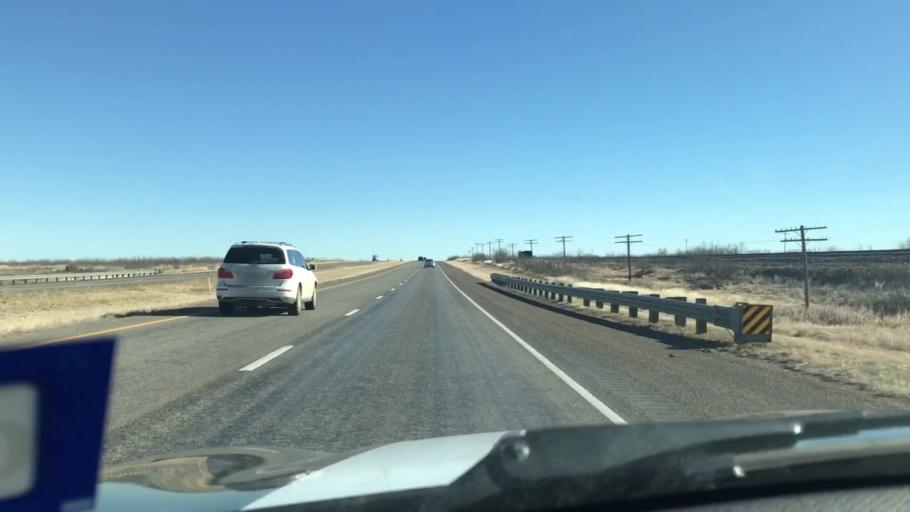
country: US
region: Texas
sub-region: Garza County
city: Post
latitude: 33.1324
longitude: -101.3032
